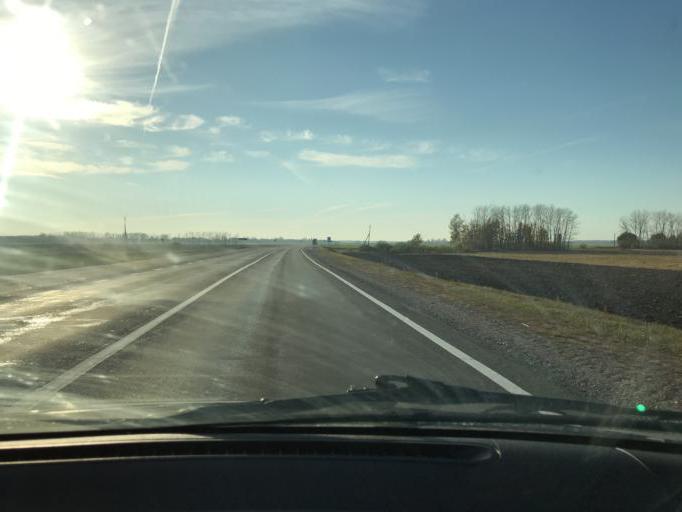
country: BY
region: Brest
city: Antopal'
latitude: 52.2096
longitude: 24.6348
